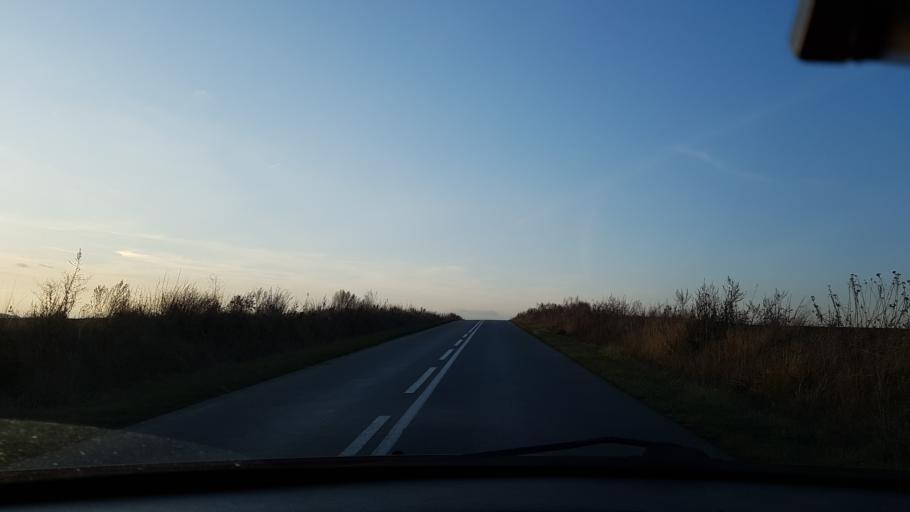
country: PL
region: Lower Silesian Voivodeship
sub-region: Powiat zabkowicki
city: Henrykow
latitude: 50.6696
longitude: 16.9707
